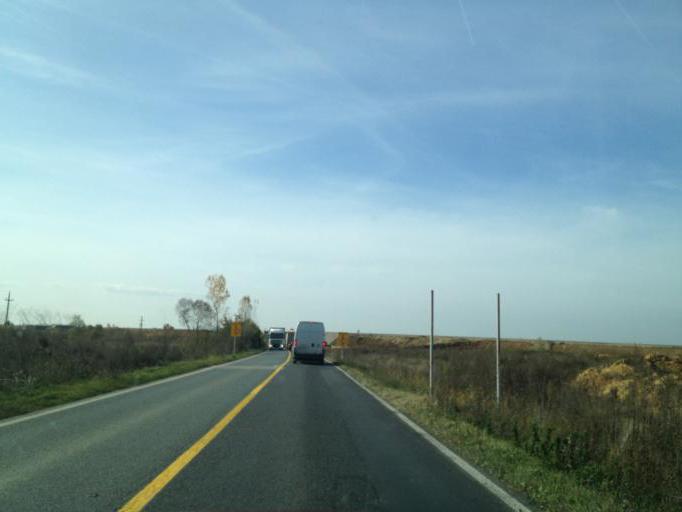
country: RO
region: Timis
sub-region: Comuna Margina
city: Margina
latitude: 45.8582
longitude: 22.2485
